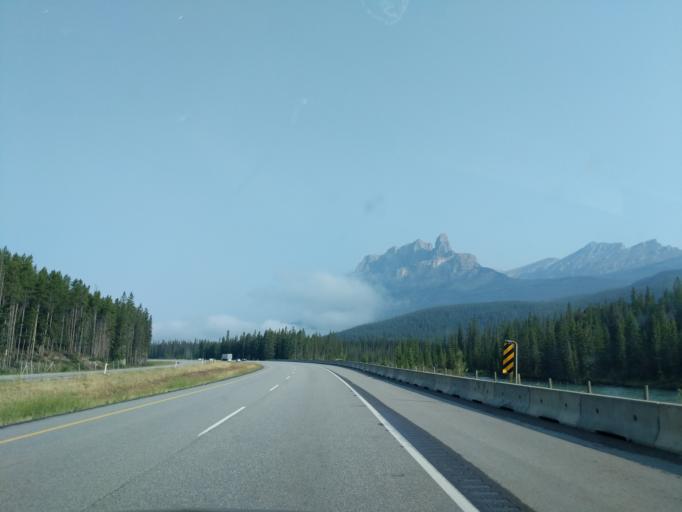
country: CA
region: Alberta
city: Banff
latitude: 51.2524
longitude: -115.8889
